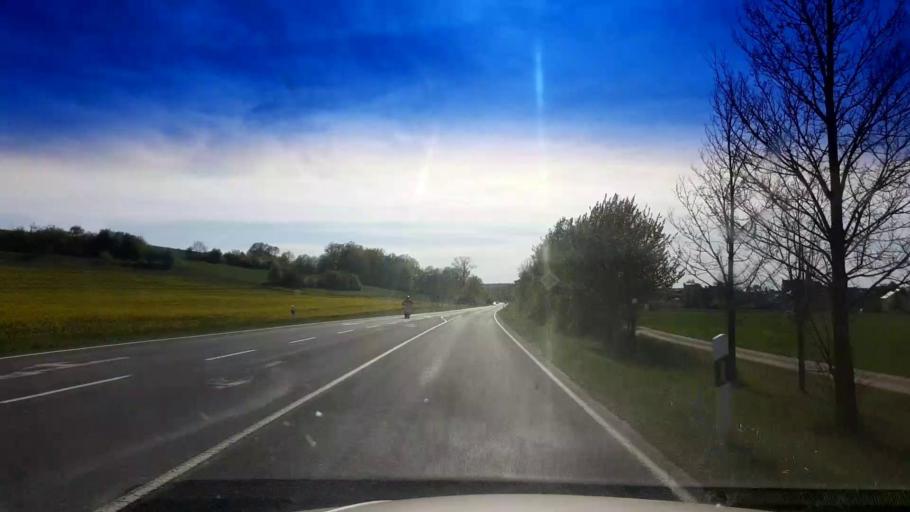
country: DE
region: Bavaria
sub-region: Upper Franconia
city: Buttenheim
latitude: 49.8025
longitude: 11.0441
